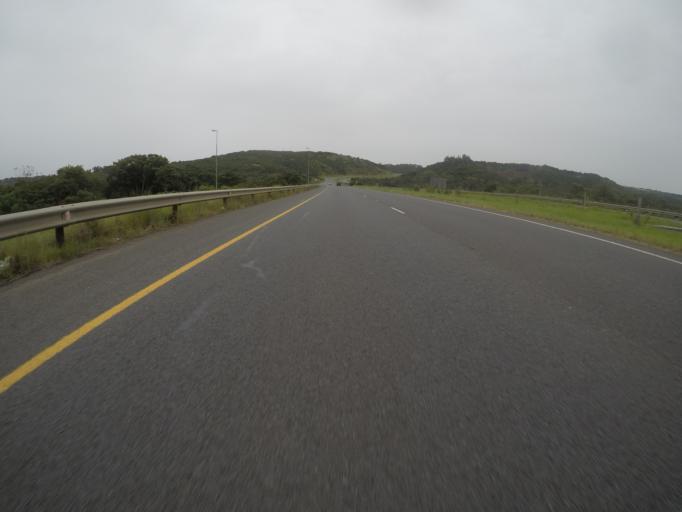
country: ZA
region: Eastern Cape
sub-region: Buffalo City Metropolitan Municipality
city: East London
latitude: -32.9642
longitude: 27.9196
